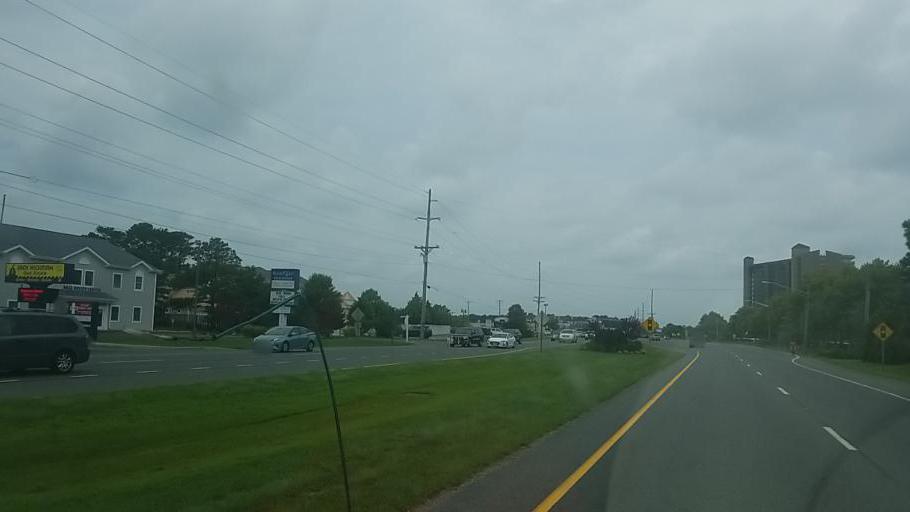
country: US
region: Delaware
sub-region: Sussex County
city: Bethany Beach
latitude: 38.5245
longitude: -75.0554
